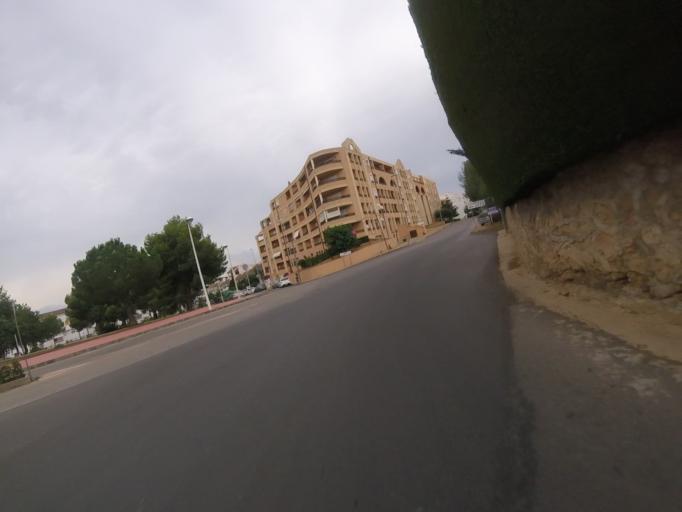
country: ES
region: Valencia
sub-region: Provincia de Castello
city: Alcoceber
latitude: 40.2568
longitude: 0.2887
